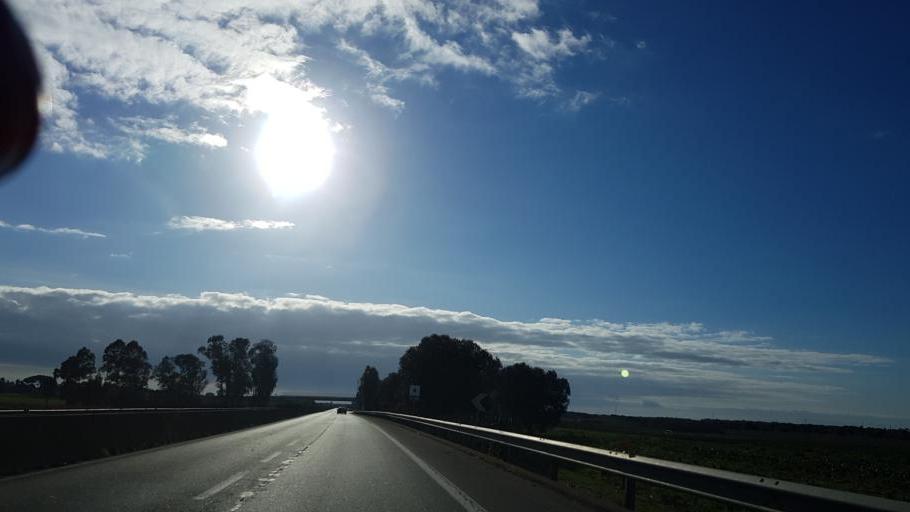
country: IT
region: Apulia
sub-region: Provincia di Brindisi
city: Tuturano
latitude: 40.5582
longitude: 17.9912
